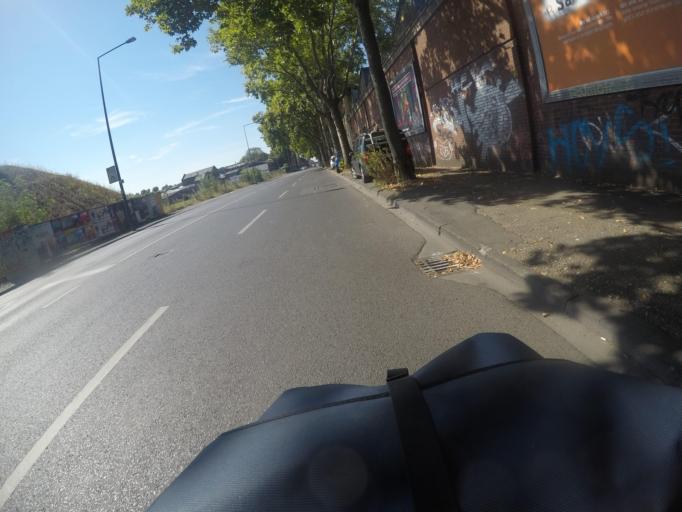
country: DE
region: North Rhine-Westphalia
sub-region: Regierungsbezirk Koln
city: Muelheim
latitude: 50.9573
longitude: 6.9941
